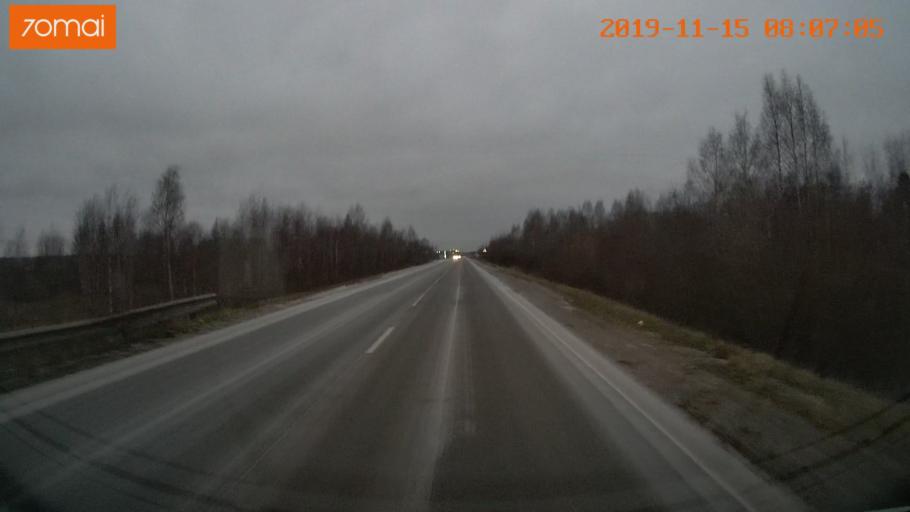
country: RU
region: Vologda
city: Cherepovets
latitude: 59.0250
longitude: 38.0238
